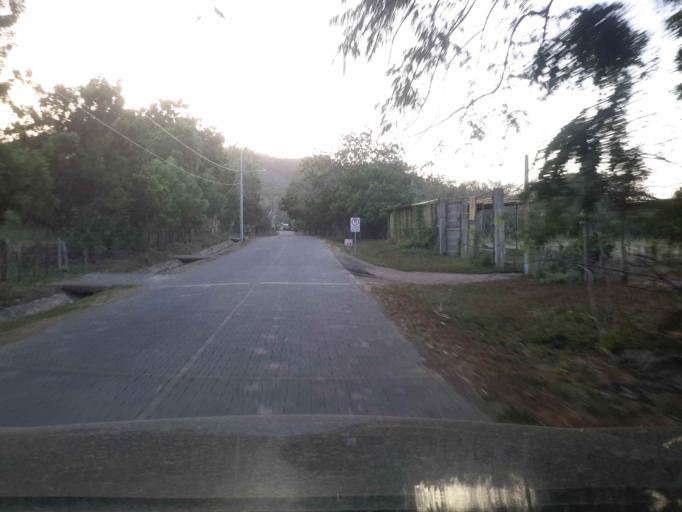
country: NI
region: Rivas
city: San Juan del Sur
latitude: 11.2449
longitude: -85.8418
